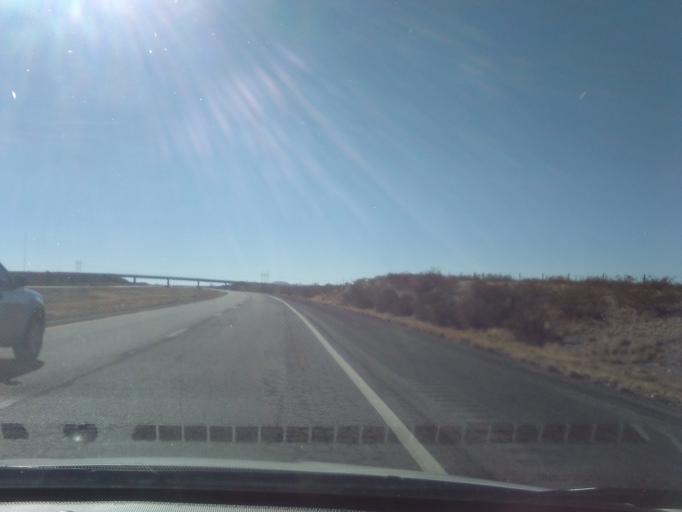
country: US
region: New Mexico
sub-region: Sierra County
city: Elephant Butte
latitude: 33.6110
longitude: -107.1504
